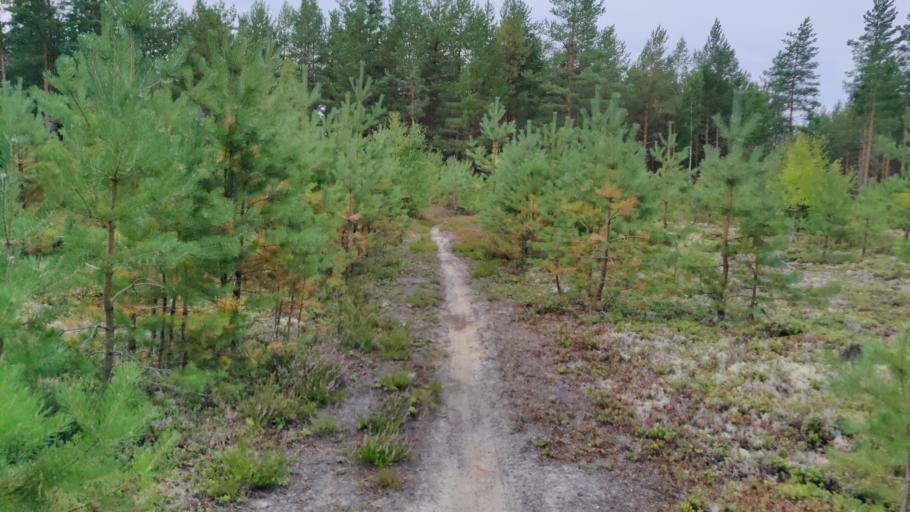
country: SE
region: Vaermland
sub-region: Hagfors Kommun
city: Hagfors
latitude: 60.0256
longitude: 13.5456
